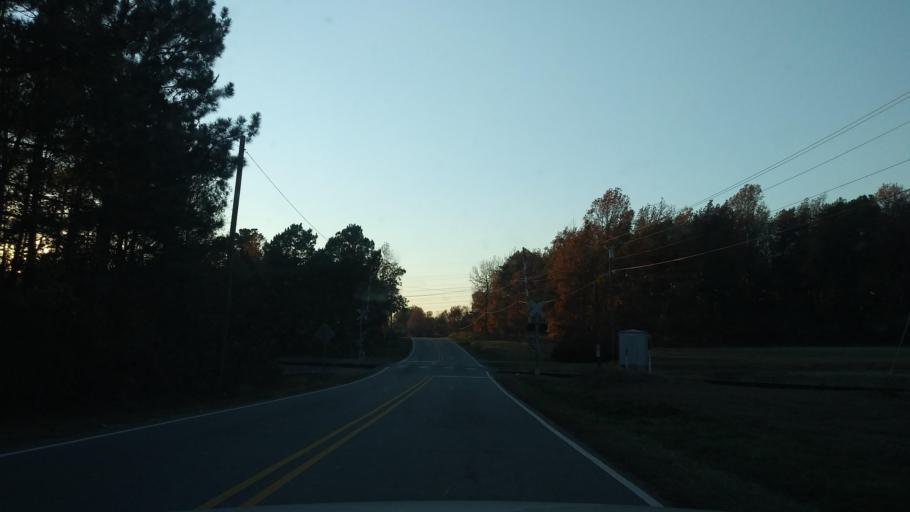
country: US
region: North Carolina
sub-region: Guilford County
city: Pleasant Garden
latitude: 35.9909
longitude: -79.7788
